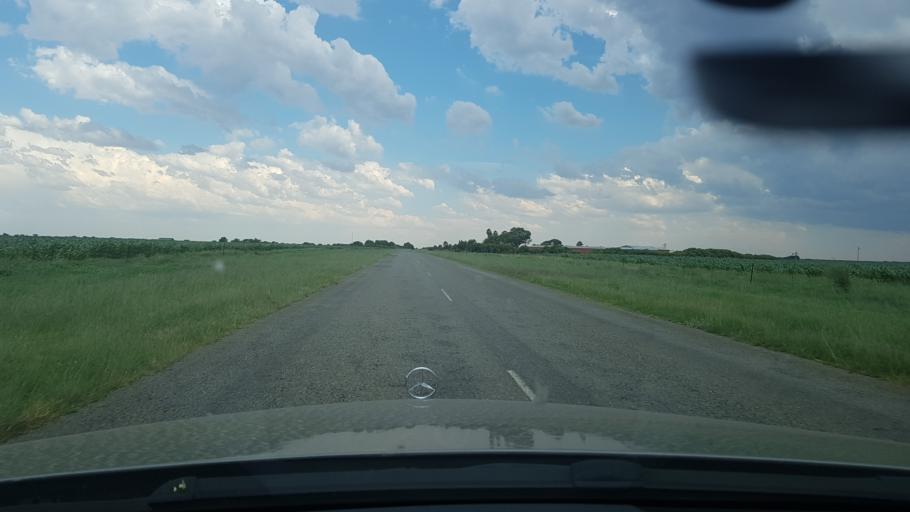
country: ZA
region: Orange Free State
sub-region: Lejweleputswa District Municipality
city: Hoopstad
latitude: -27.9154
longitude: 25.6830
